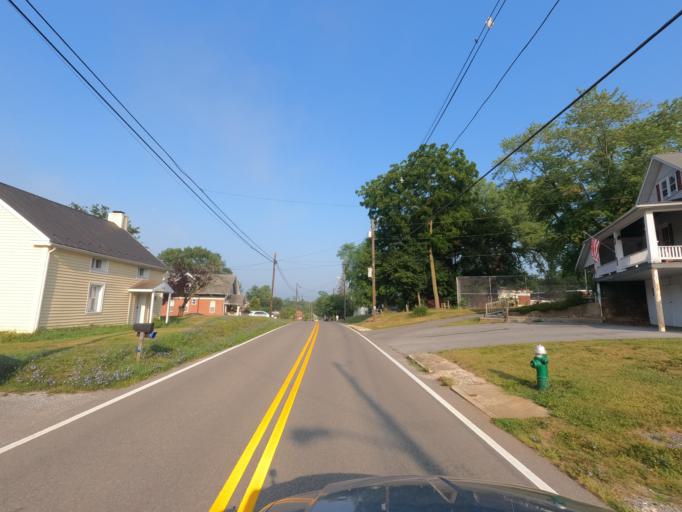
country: US
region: Maryland
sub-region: Washington County
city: Robinwood
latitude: 39.6431
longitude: -77.6391
